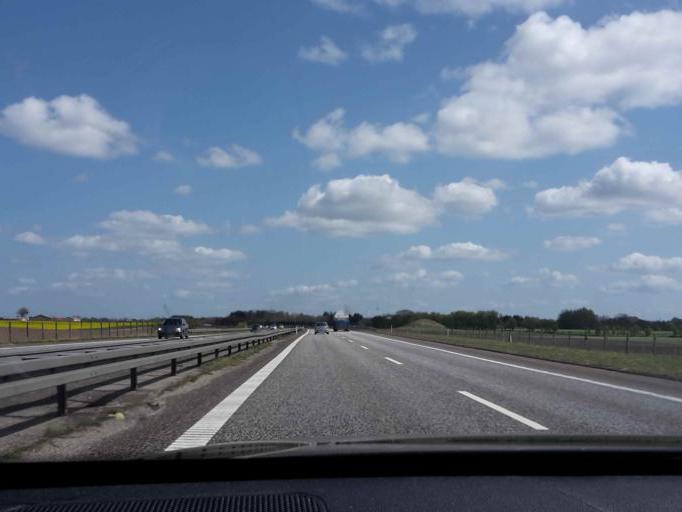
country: DK
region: South Denmark
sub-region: Vejen Kommune
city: Vejen
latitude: 55.4977
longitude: 9.2160
